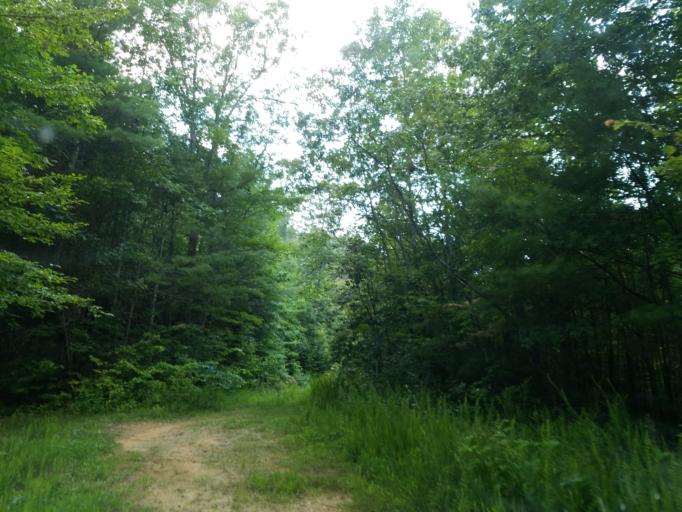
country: US
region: Georgia
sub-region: Union County
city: Blairsville
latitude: 34.7457
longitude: -84.0677
